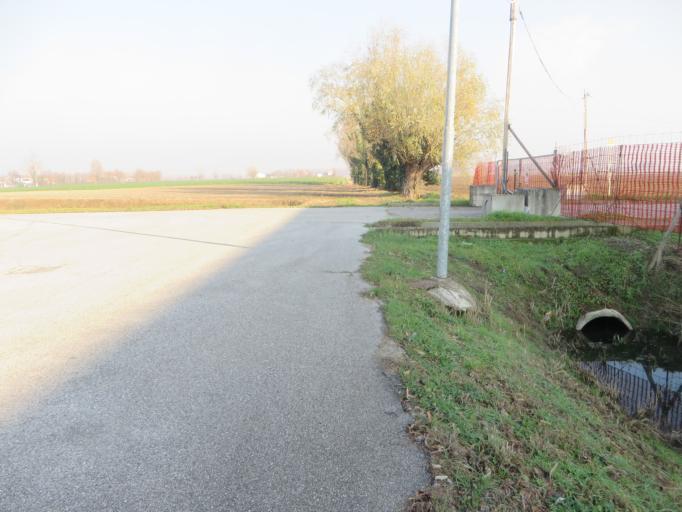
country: IT
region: Veneto
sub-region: Provincia di Verona
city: San Pietro di Morubio
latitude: 45.2257
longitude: 11.2446
